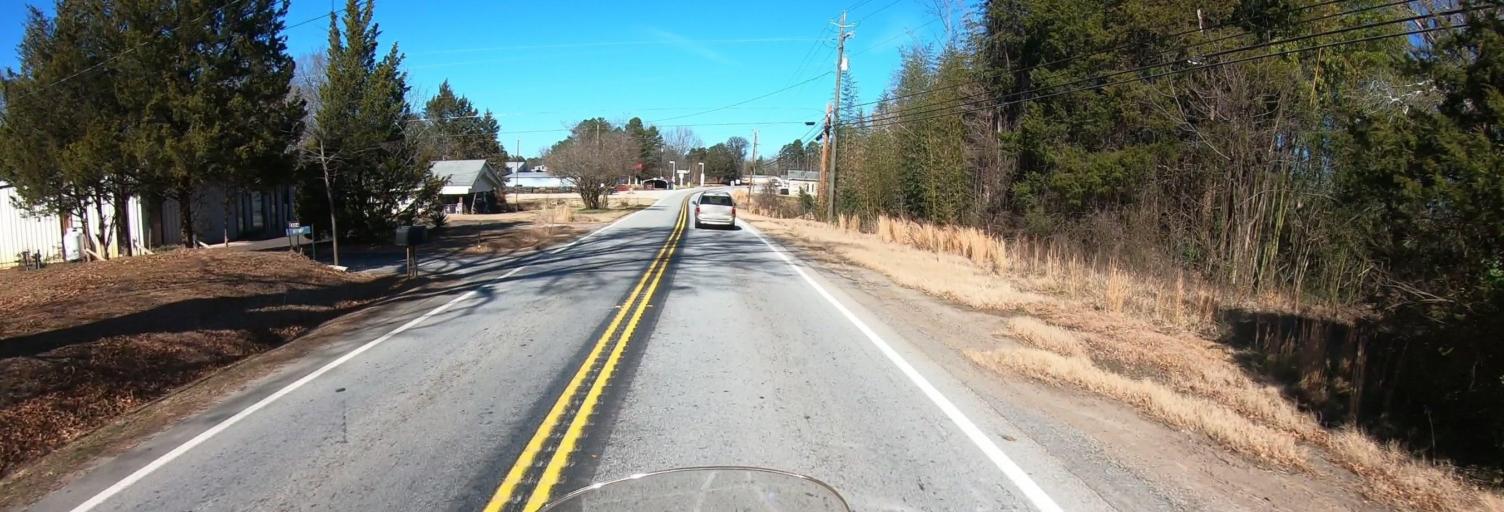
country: US
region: Georgia
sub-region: Stephens County
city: Toccoa
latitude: 34.5672
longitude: -83.3460
